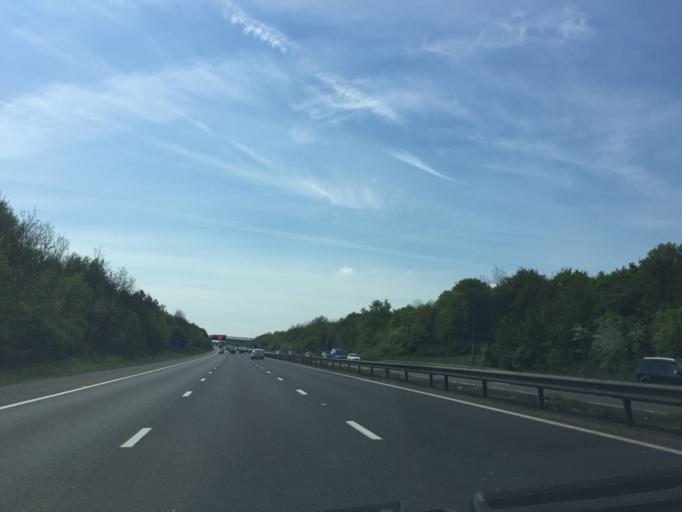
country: GB
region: England
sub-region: Essex
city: Chigwell
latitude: 51.6372
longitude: 0.0791
